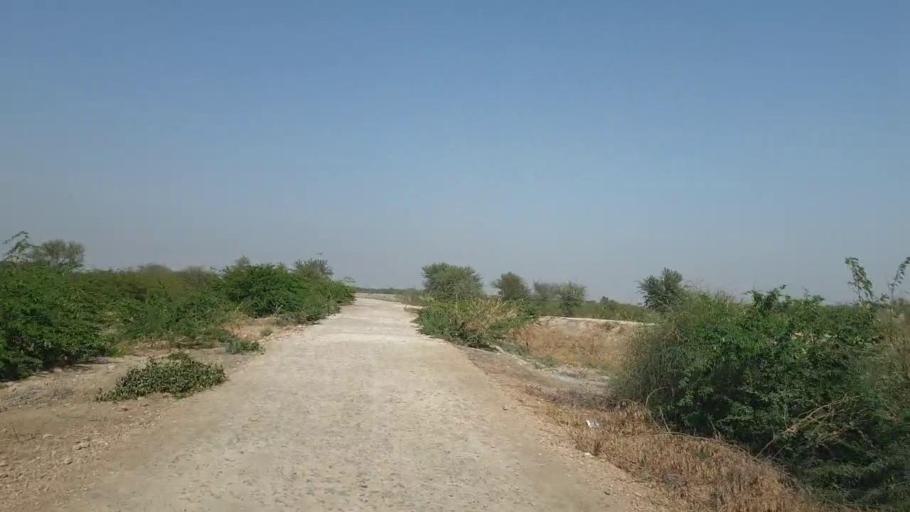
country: PK
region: Sindh
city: Nabisar
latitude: 24.9965
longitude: 69.5286
